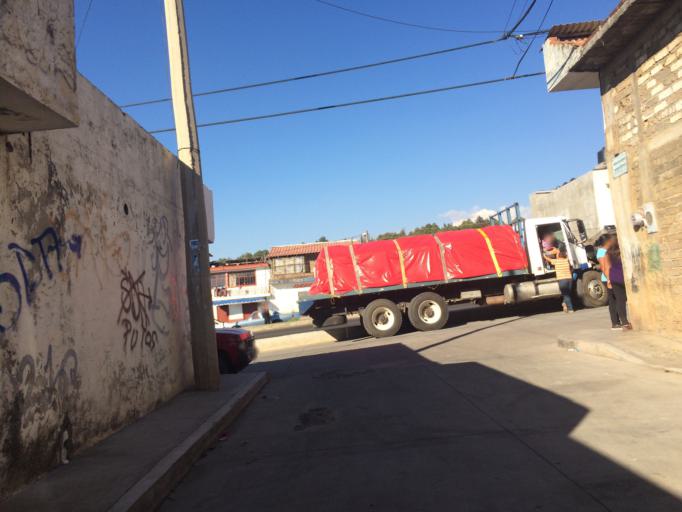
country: MX
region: Michoacan
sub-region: Patzcuaro
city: Colonia Vista Bella (Lomas del Peaje)
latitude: 19.4997
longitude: -101.6016
